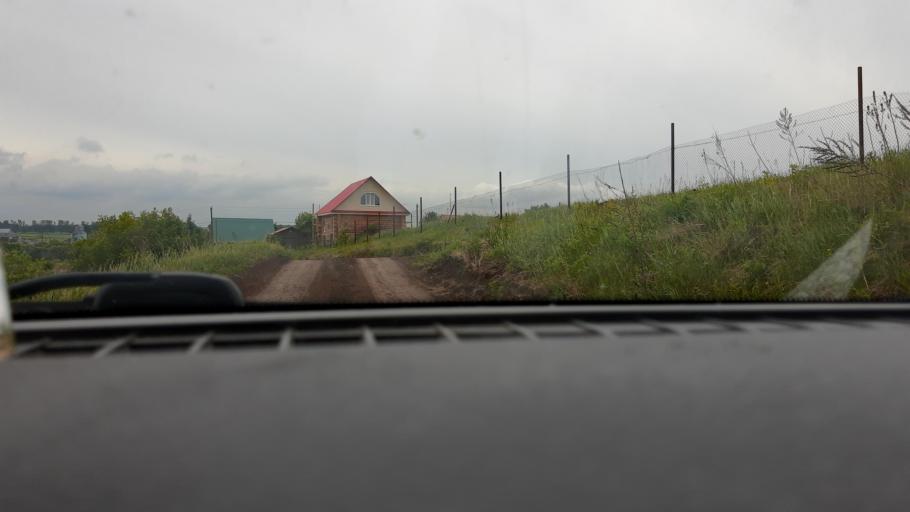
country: RU
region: Bashkortostan
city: Chishmy
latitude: 54.6857
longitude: 55.4833
